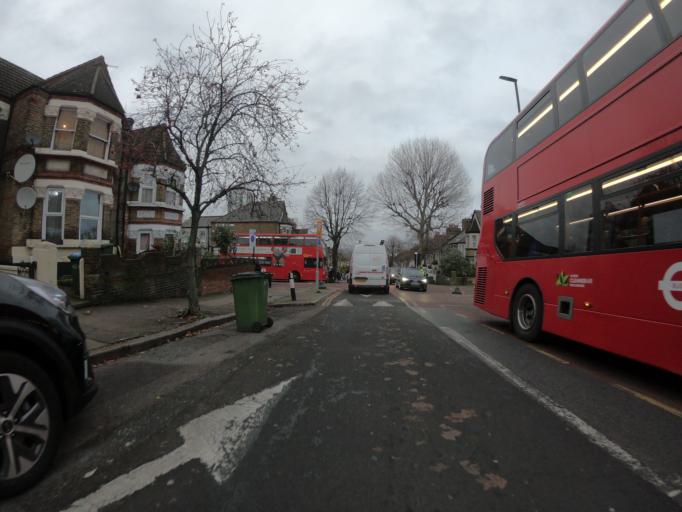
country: GB
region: England
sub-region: Greater London
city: Woolwich
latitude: 51.4855
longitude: 0.0839
